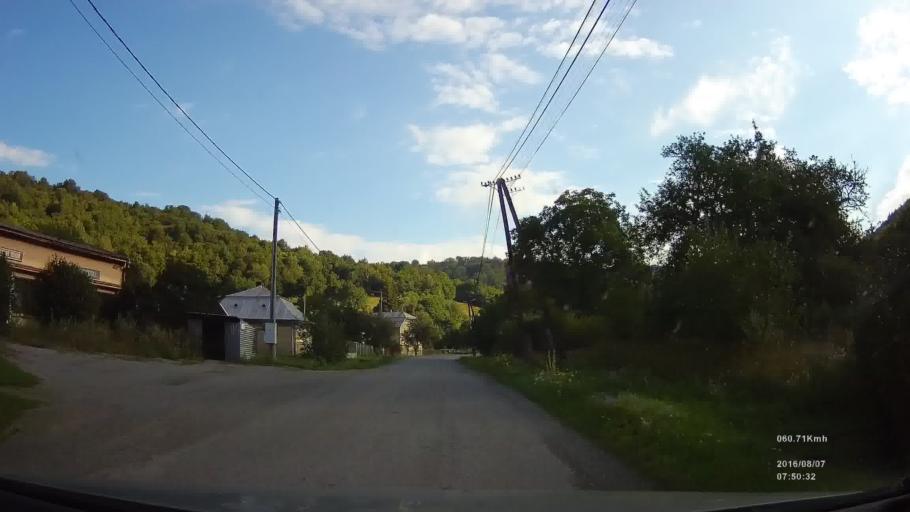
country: SK
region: Presovsky
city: Medzilaborce
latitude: 49.3002
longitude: 21.7779
